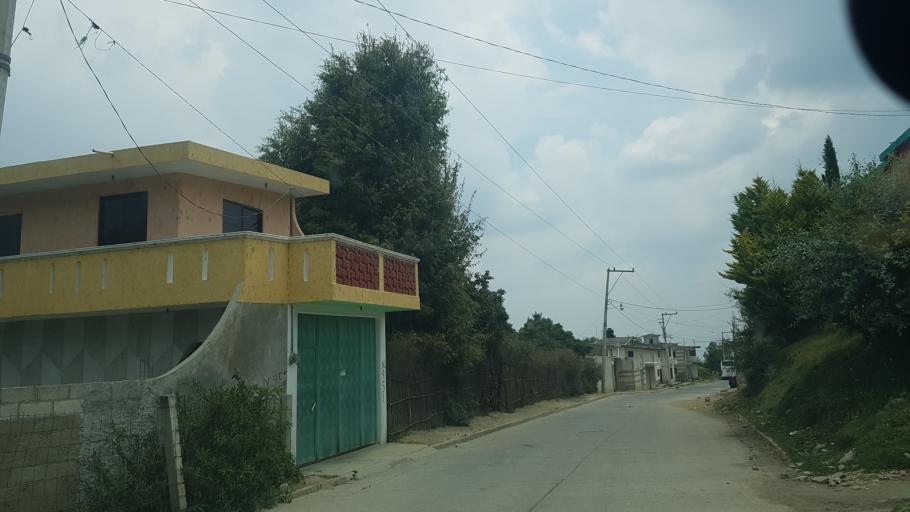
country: MX
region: Puebla
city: Domingo Arenas
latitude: 19.1530
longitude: -98.5045
